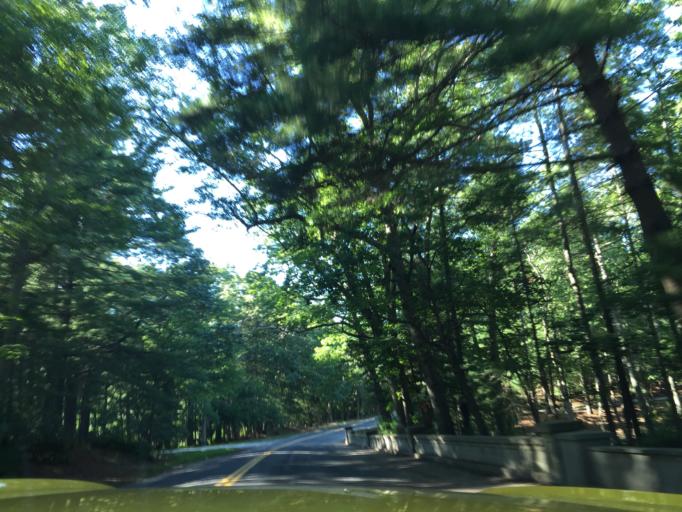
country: US
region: New York
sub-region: Suffolk County
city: Southold
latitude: 41.0417
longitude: -72.3917
